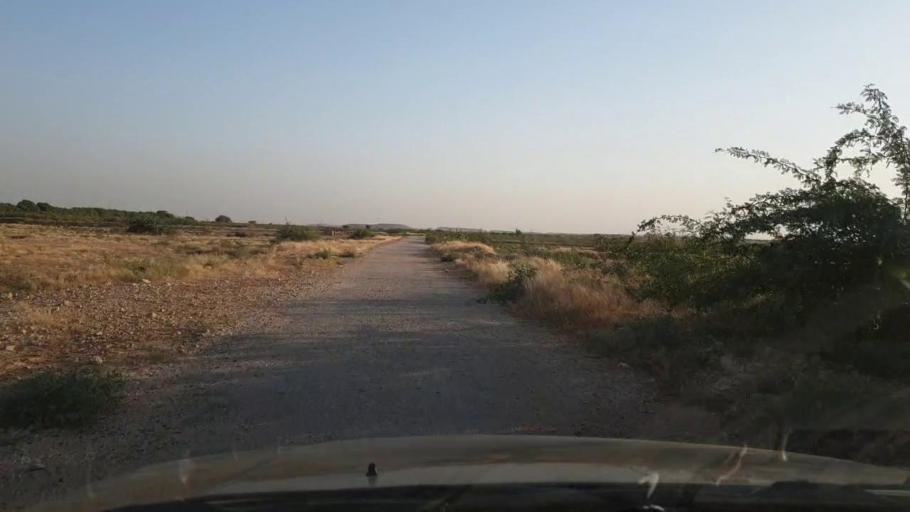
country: PK
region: Sindh
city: Kotri
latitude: 25.2276
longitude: 68.2247
